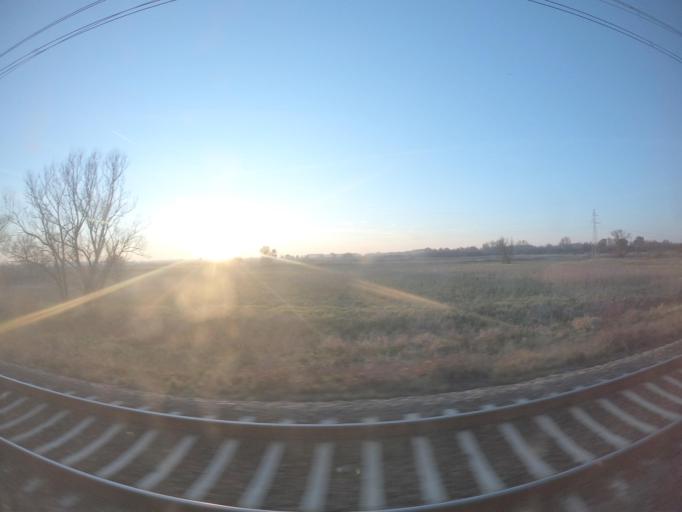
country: PL
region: Lubusz
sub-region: Powiat gorzowski
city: Kostrzyn nad Odra
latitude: 52.5630
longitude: 14.6477
